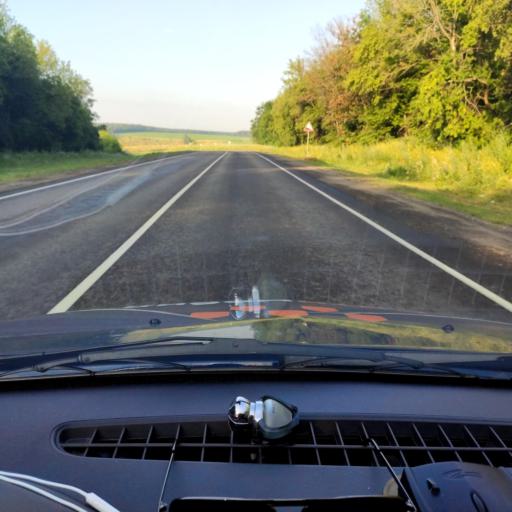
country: RU
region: Lipetsk
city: Izmalkovo
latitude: 52.4662
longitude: 38.0163
